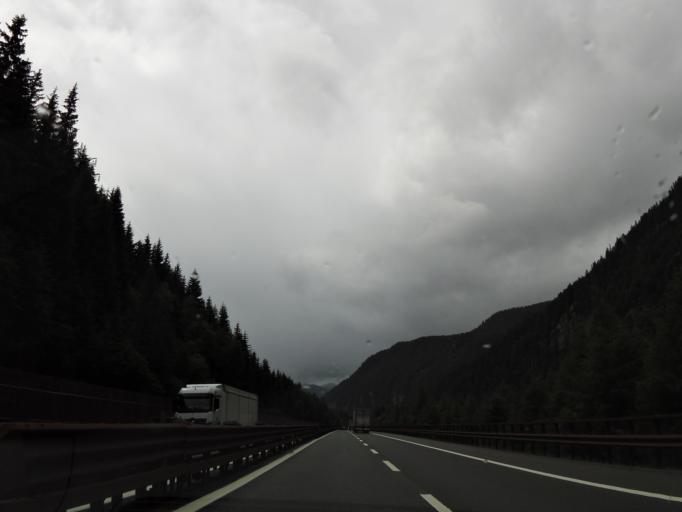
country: IT
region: Trentino-Alto Adige
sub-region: Bolzano
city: Colle Isarco
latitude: 46.9782
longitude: 11.4855
